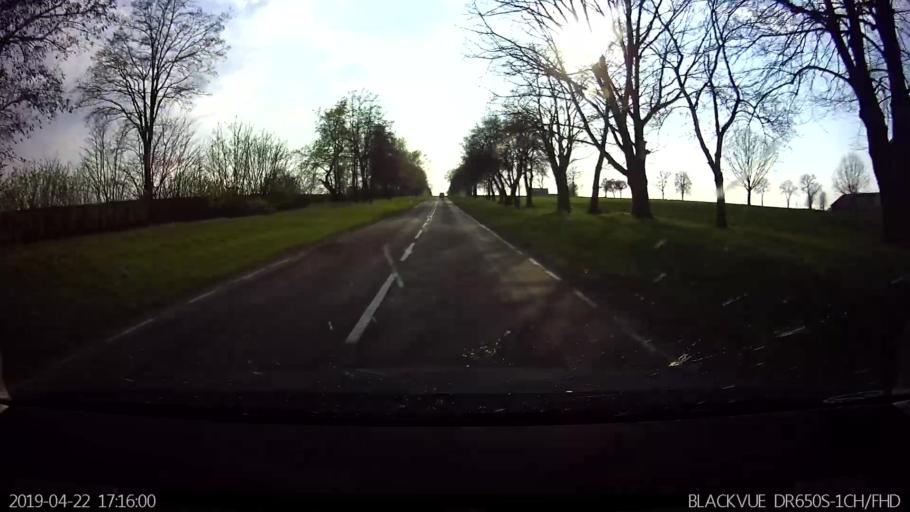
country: PL
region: Masovian Voivodeship
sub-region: Powiat sokolowski
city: Repki
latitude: 52.3972
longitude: 22.4727
